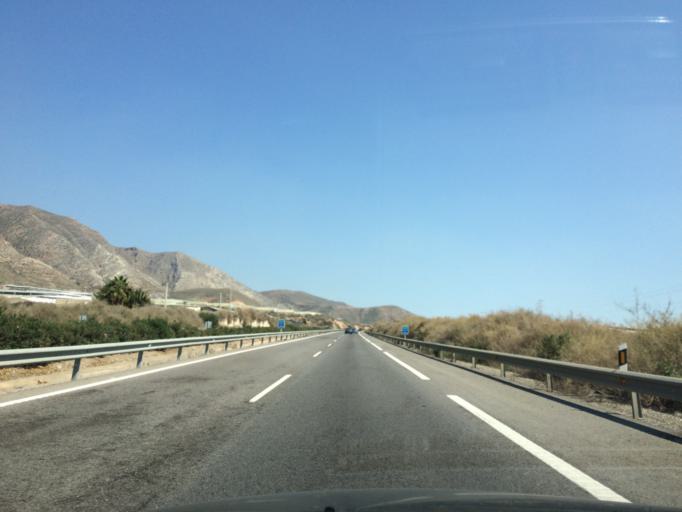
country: ES
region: Andalusia
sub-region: Provincia de Almeria
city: Adra
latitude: 36.7649
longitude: -2.9595
